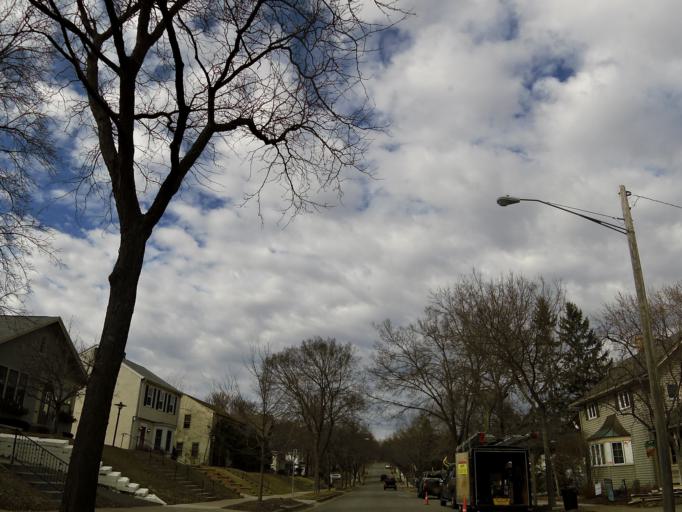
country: US
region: Minnesota
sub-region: Hennepin County
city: Edina
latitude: 44.9167
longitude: -93.3152
